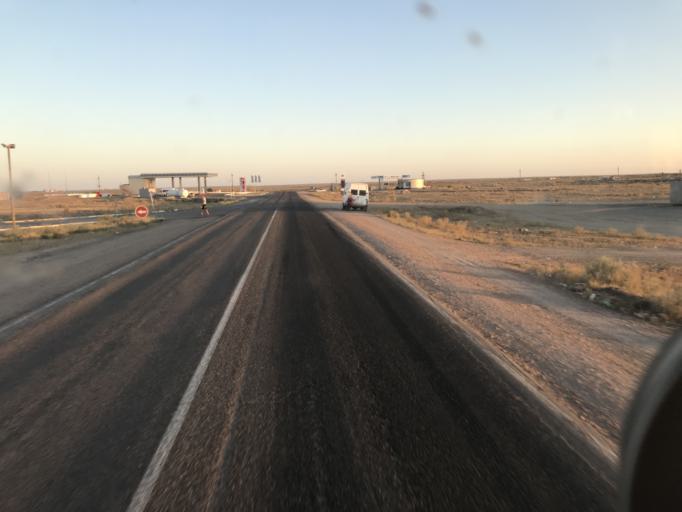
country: KZ
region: Qaraghandy
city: Saryshaghan
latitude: 46.0217
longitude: 73.5914
